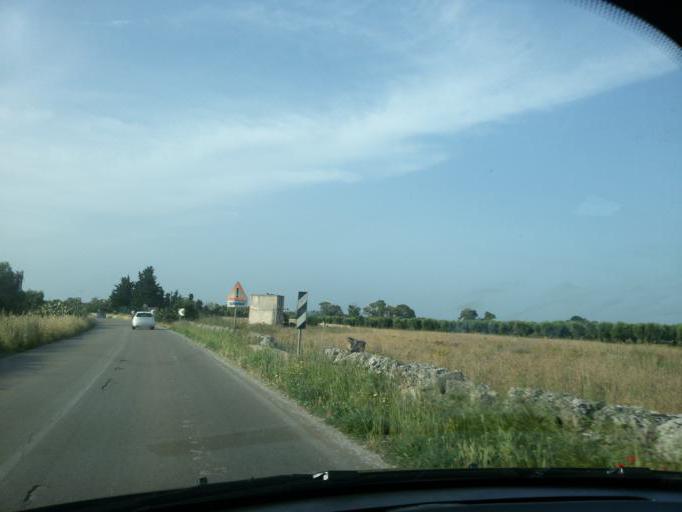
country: IT
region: Apulia
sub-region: Provincia di Lecce
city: Porto Cesareo
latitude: 40.3077
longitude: 17.8629
